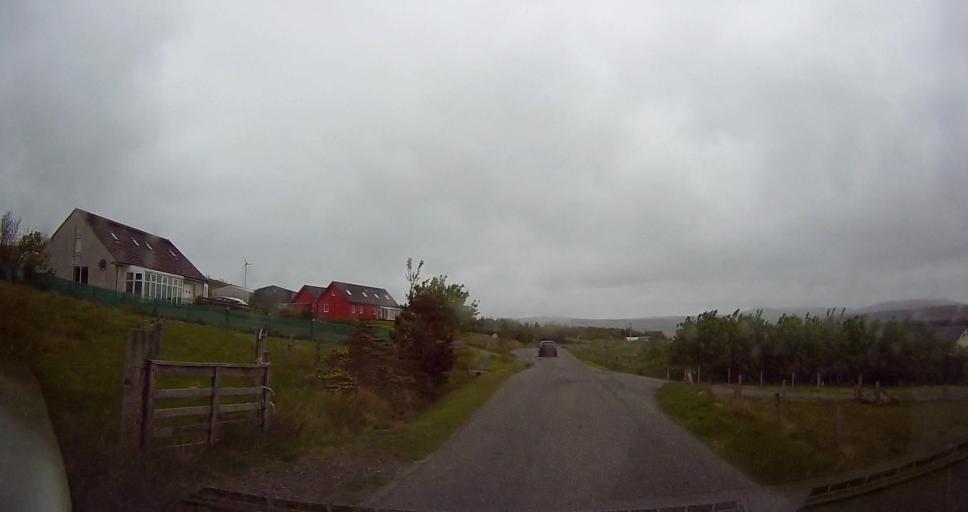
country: GB
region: Scotland
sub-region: Shetland Islands
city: Lerwick
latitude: 60.2827
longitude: -1.3882
